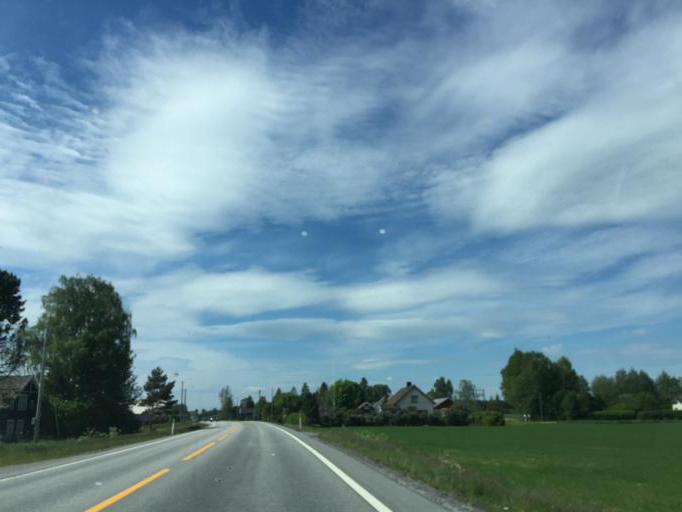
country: NO
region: Hedmark
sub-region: Sor-Odal
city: Skarnes
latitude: 60.2183
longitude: 11.6401
